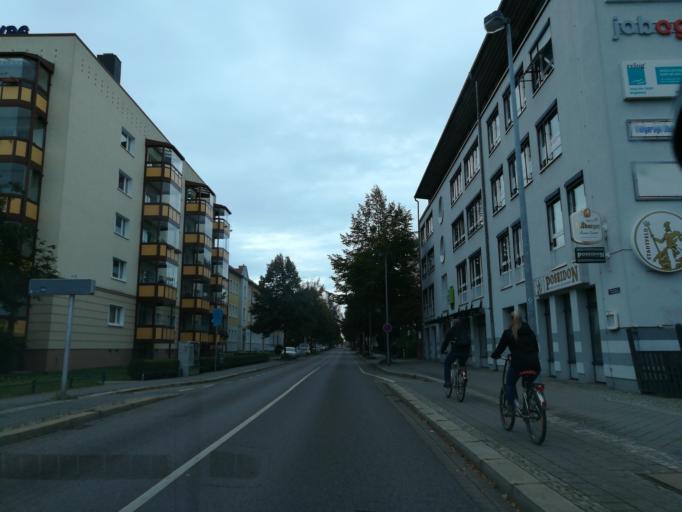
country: DE
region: Saxony-Anhalt
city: Magdeburg
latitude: 52.1356
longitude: 11.6169
